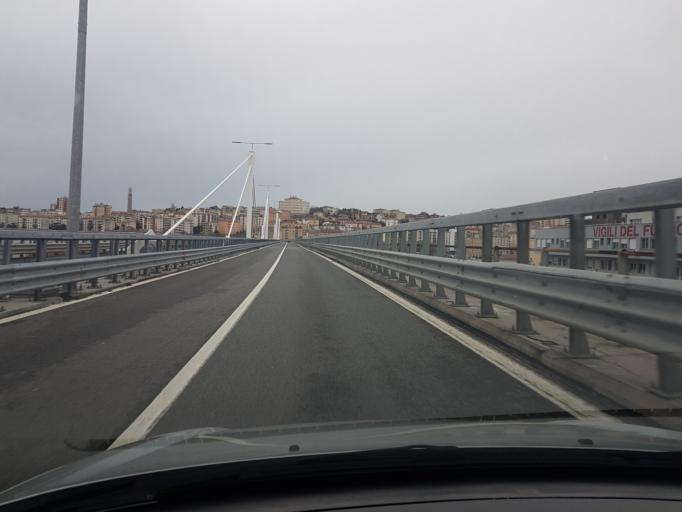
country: IT
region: Friuli Venezia Giulia
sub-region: Provincia di Trieste
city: Trieste
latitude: 45.6357
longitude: 13.7790
